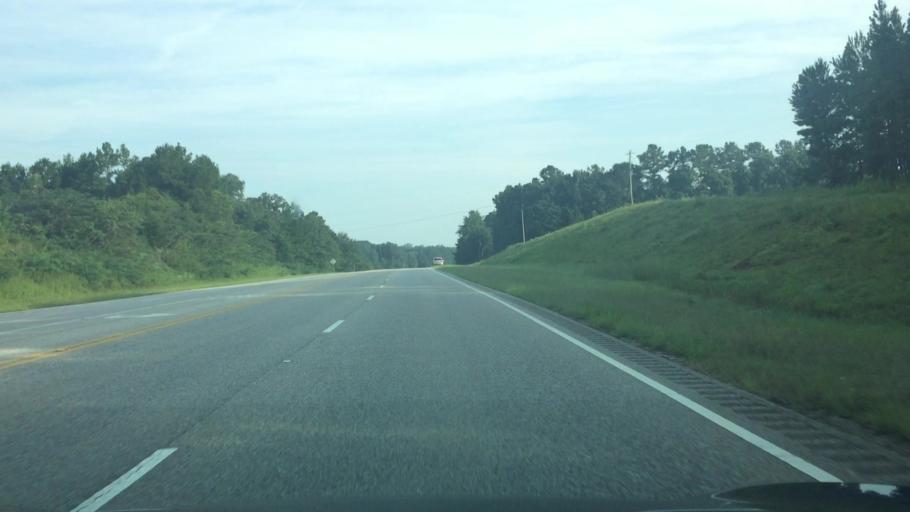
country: US
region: Alabama
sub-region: Covington County
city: Andalusia
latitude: 31.4160
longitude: -86.6082
